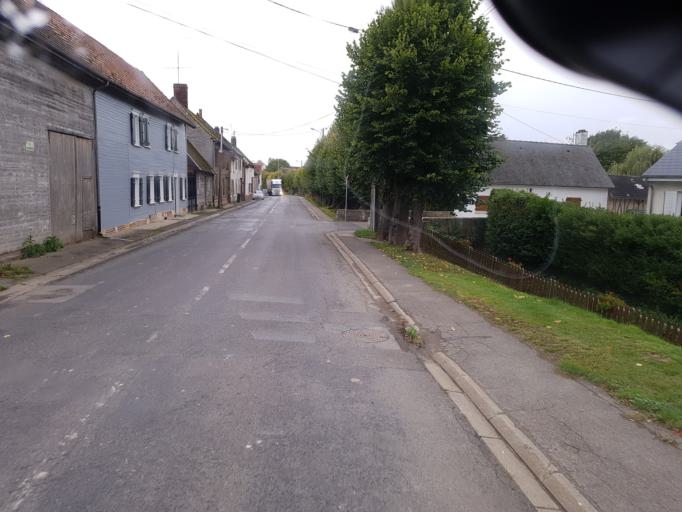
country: FR
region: Picardie
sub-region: Departement de l'Oise
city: Breteuil
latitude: 49.6662
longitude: 2.3233
